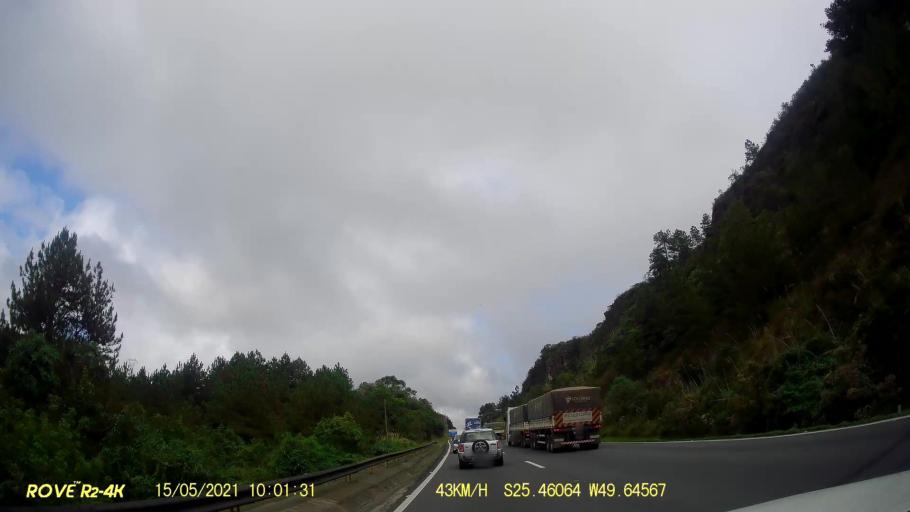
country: BR
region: Parana
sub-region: Campo Largo
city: Campo Largo
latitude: -25.4606
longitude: -49.6457
